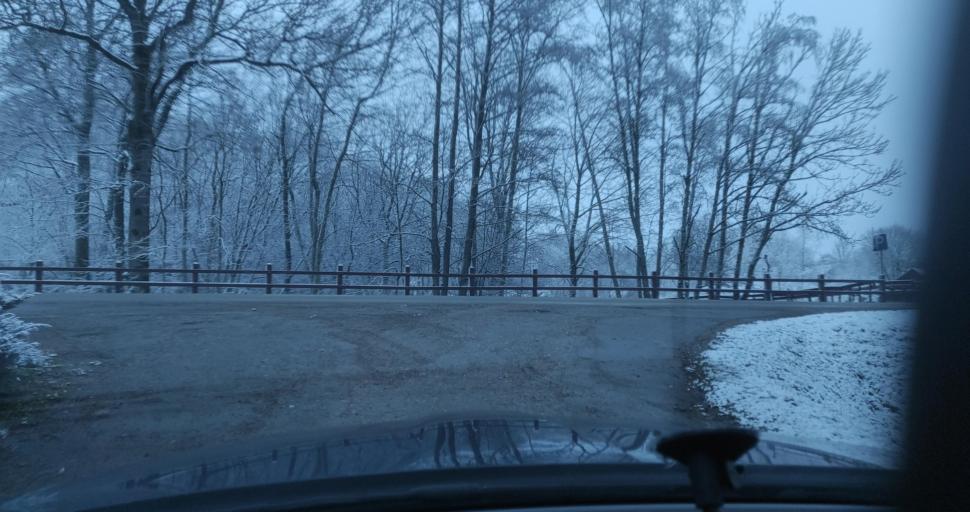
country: LV
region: Skrunda
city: Skrunda
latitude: 56.8725
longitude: 22.2365
